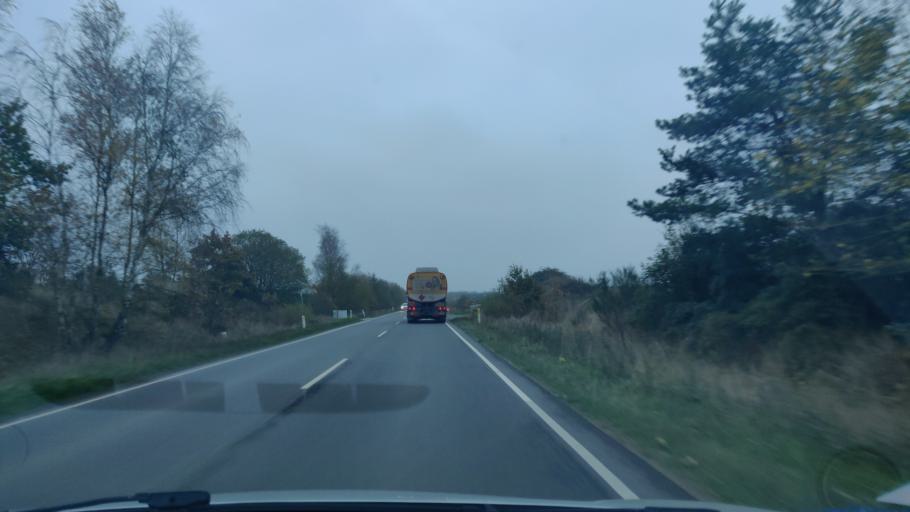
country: DK
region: South Denmark
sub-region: Kolding Kommune
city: Kolding
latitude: 55.5706
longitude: 9.4217
